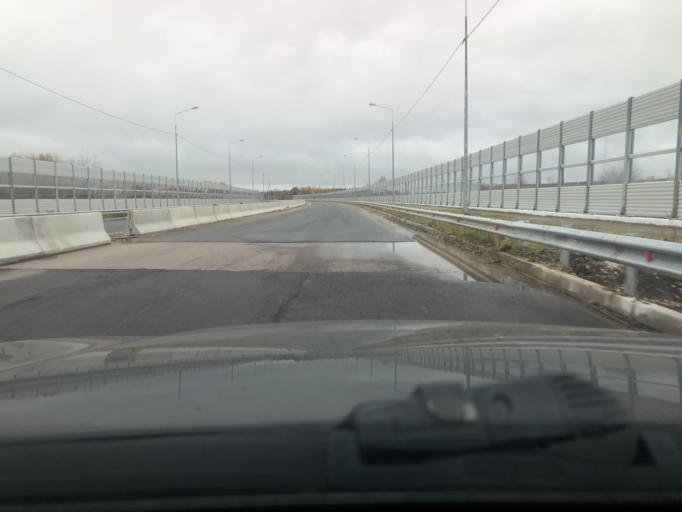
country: RU
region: Moskovskaya
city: Semkhoz
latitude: 56.3153
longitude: 38.0910
